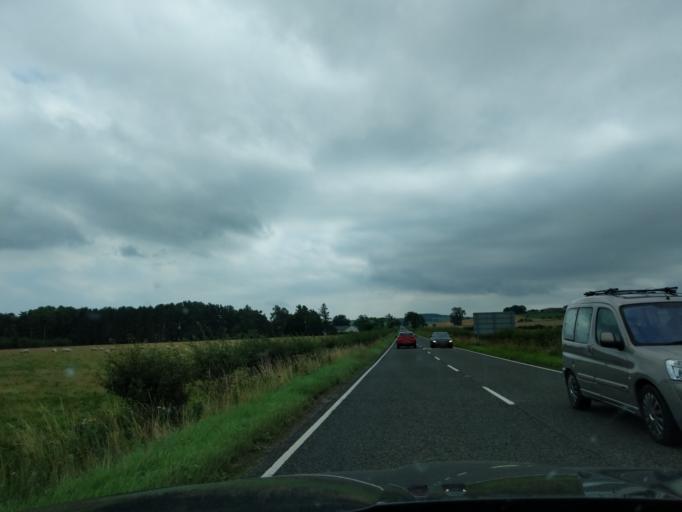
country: GB
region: England
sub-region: Northumberland
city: Whittingham
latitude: 55.4013
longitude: -1.8611
